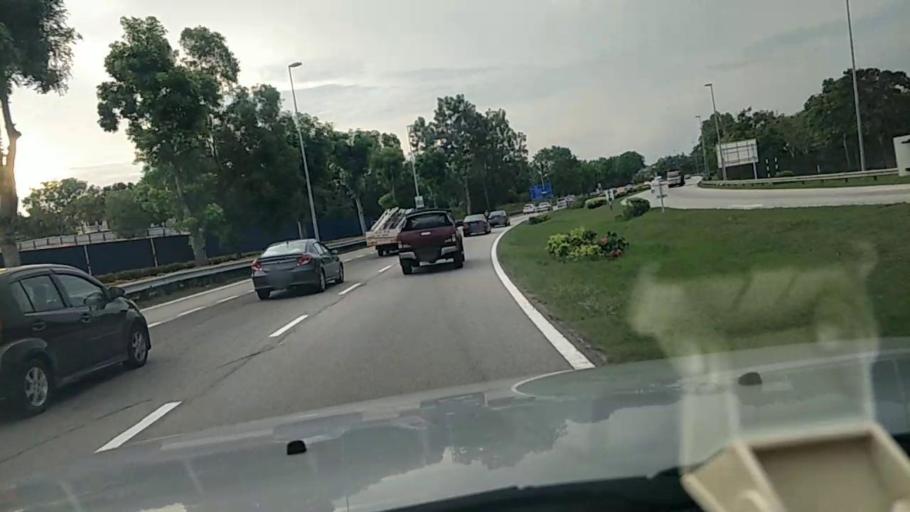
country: MY
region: Selangor
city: Shah Alam
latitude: 3.0999
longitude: 101.4756
